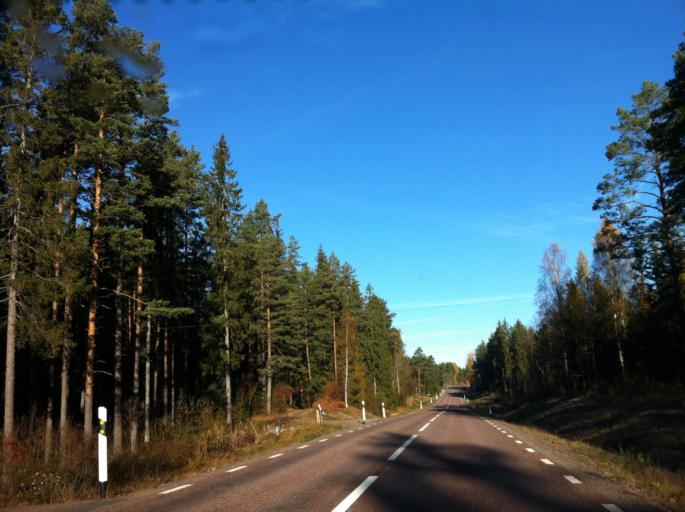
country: SE
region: Gaevleborg
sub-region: Gavle Kommun
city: Gavle
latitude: 60.5461
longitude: 17.1295
